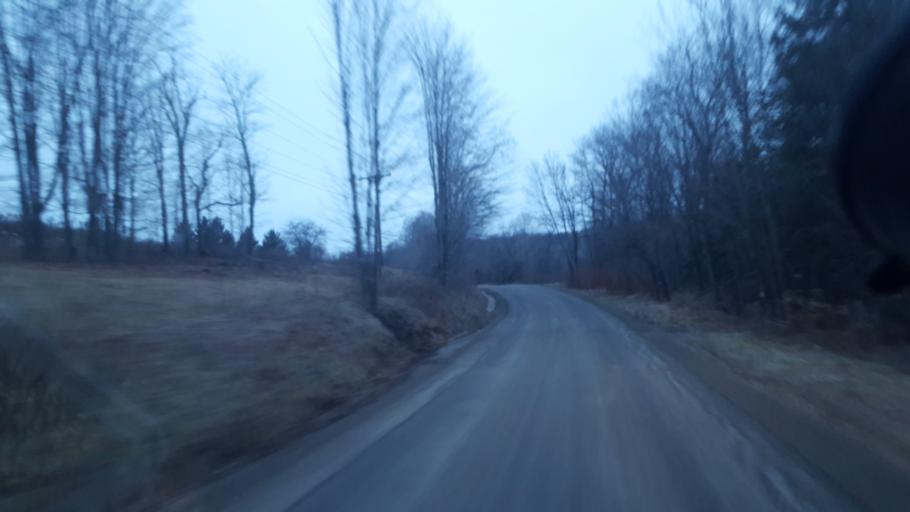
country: US
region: Pennsylvania
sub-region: Tioga County
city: Westfield
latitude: 41.9713
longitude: -77.7233
